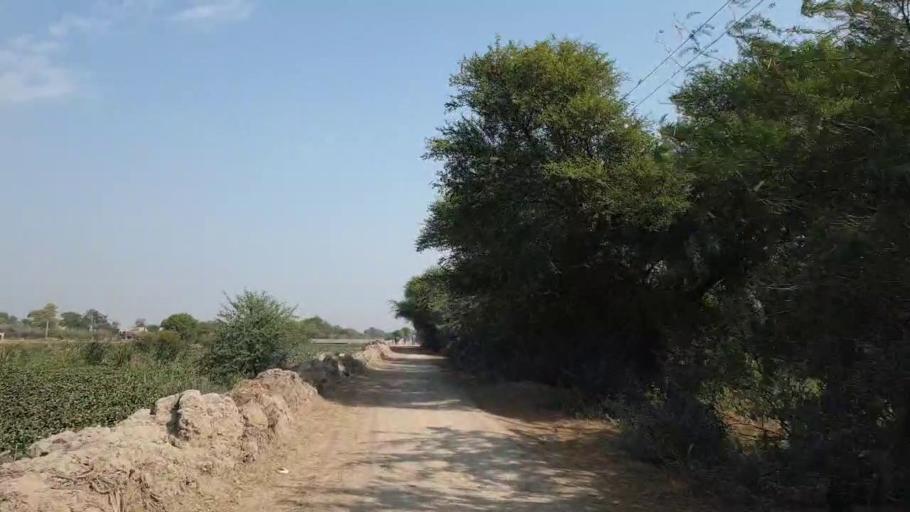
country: PK
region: Sindh
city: Tando Muhammad Khan
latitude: 25.0765
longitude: 68.4195
